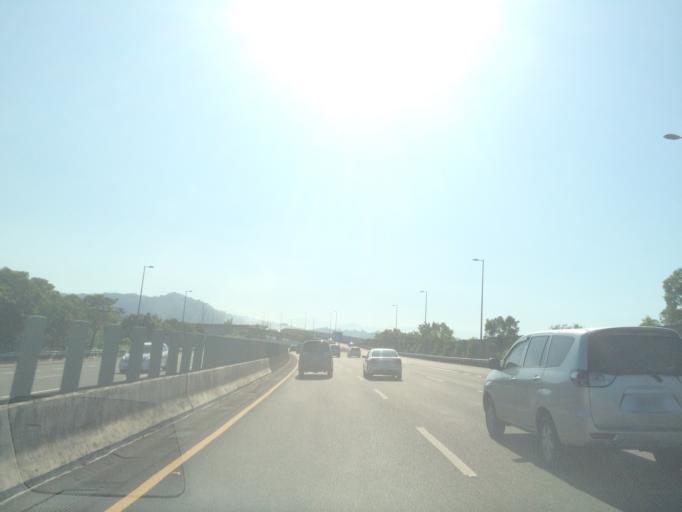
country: TW
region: Taiwan
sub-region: Nantou
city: Nantou
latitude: 23.9048
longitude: 120.7036
